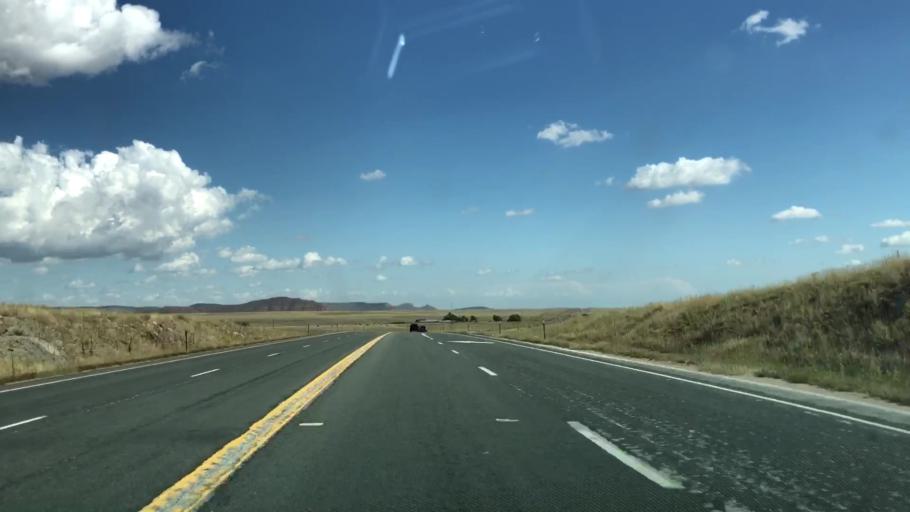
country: US
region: Colorado
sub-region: Larimer County
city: Laporte
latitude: 40.9231
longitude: -105.3390
